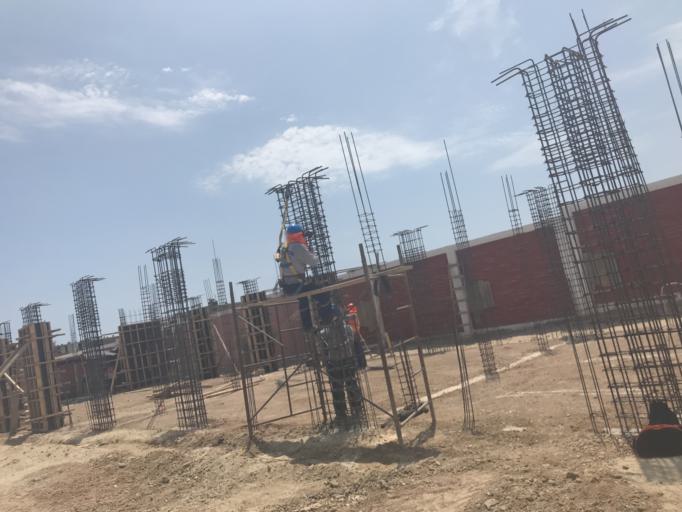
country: PE
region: Ica
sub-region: Provincia de Pisco
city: Villa Tupac Amaru
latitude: -13.8339
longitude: -76.1405
